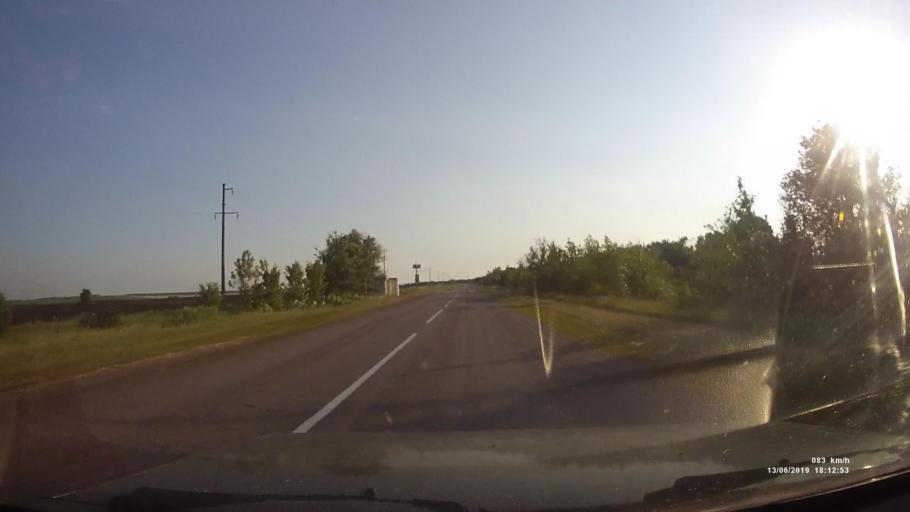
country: RU
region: Rostov
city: Kazanskaya
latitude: 49.9425
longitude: 41.4036
